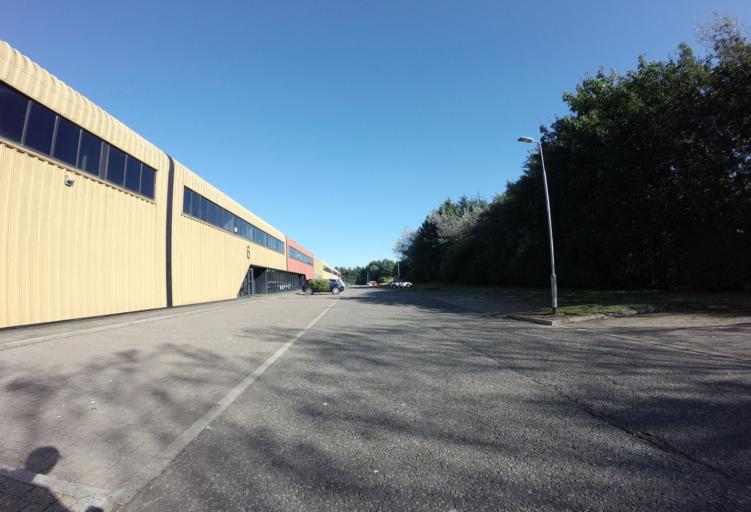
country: GB
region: Scotland
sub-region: West Lothian
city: West Calder
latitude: 55.8959
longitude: -3.5753
